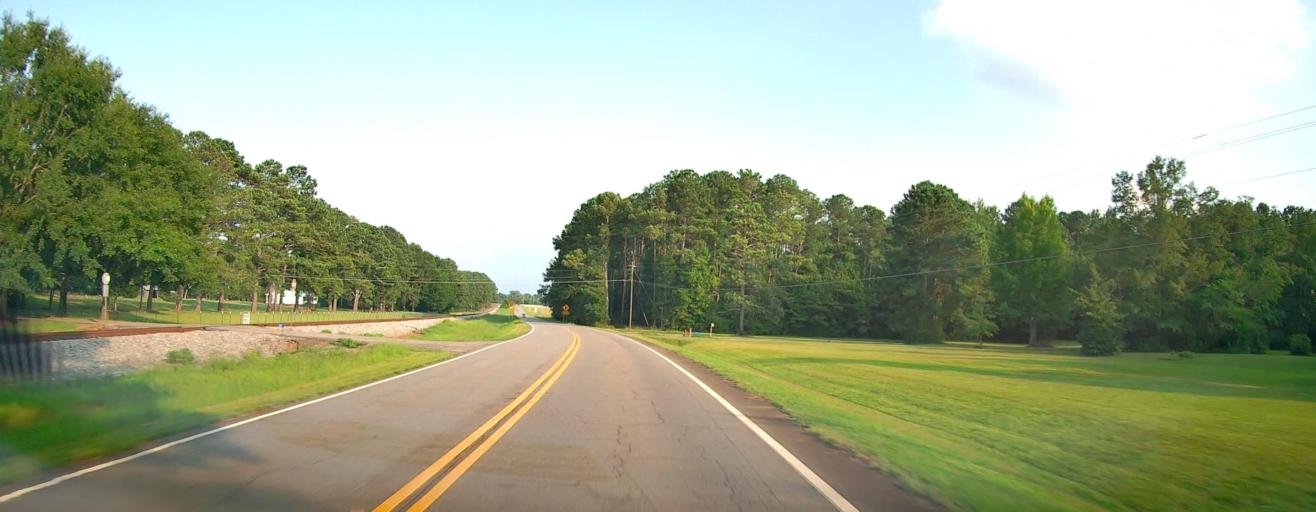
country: US
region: Georgia
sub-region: Jones County
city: Gray
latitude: 33.0482
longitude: -83.5563
